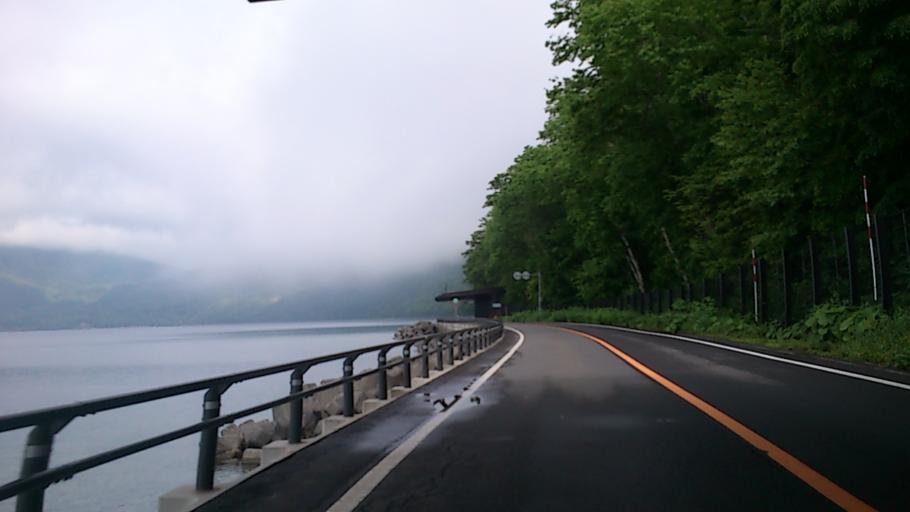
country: JP
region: Hokkaido
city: Shiraoi
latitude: 42.7946
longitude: 141.3660
